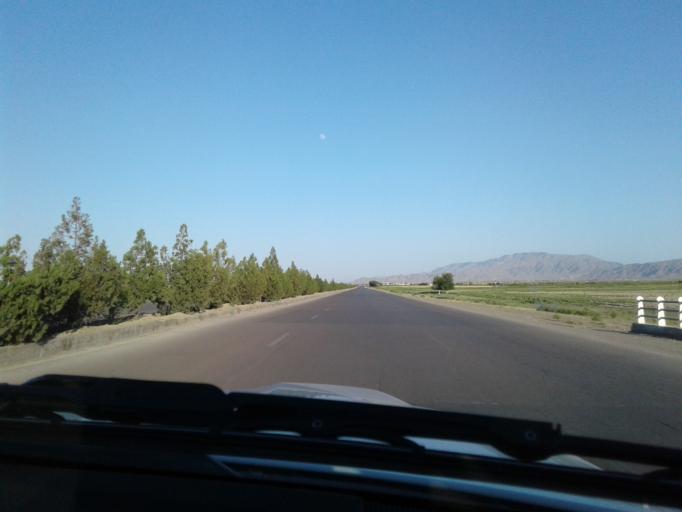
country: TM
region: Ahal
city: Baharly
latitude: 38.3472
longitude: 57.5536
